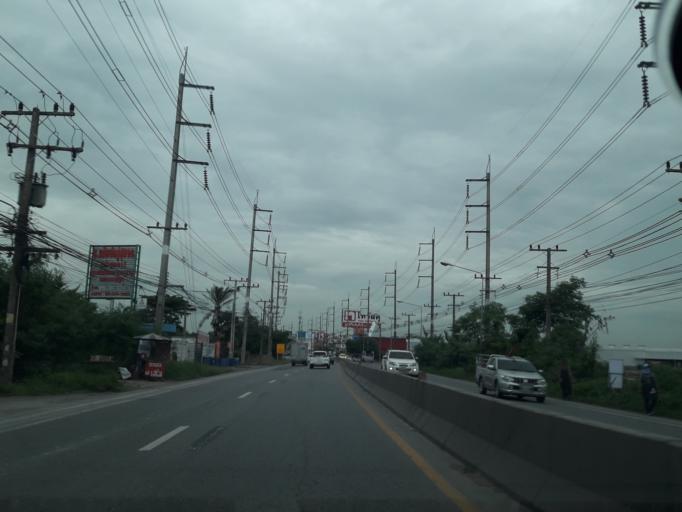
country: TH
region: Pathum Thani
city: Lam Luk Ka
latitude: 13.9383
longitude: 100.7567
